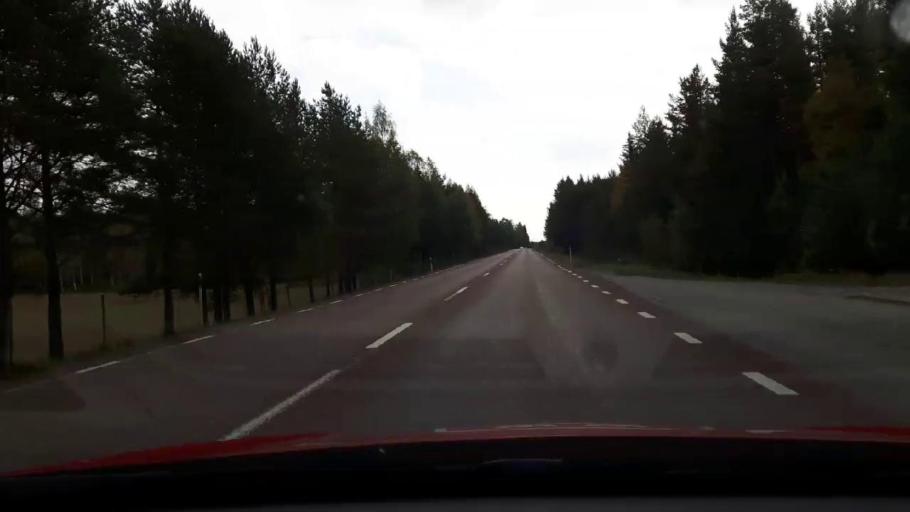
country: SE
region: Gaevleborg
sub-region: Bollnas Kommun
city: Kilafors
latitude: 61.2668
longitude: 16.5454
